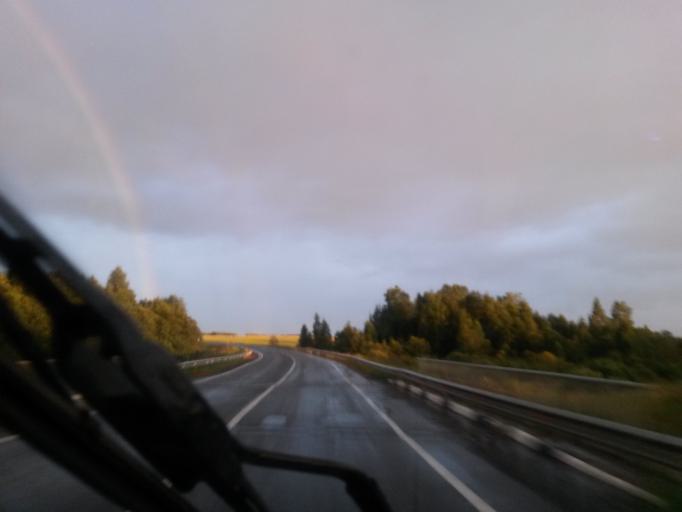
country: RU
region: Jaroslavl
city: Gavrilov-Yam
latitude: 57.3292
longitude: 39.9212
